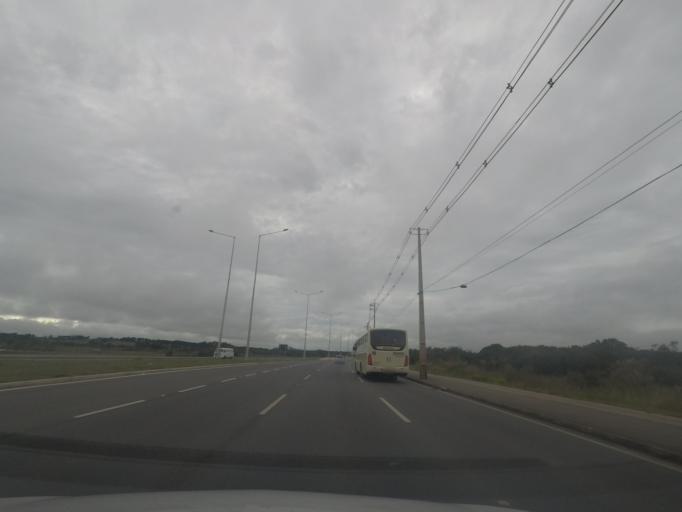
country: BR
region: Parana
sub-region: Pinhais
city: Pinhais
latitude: -25.4434
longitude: -49.1463
